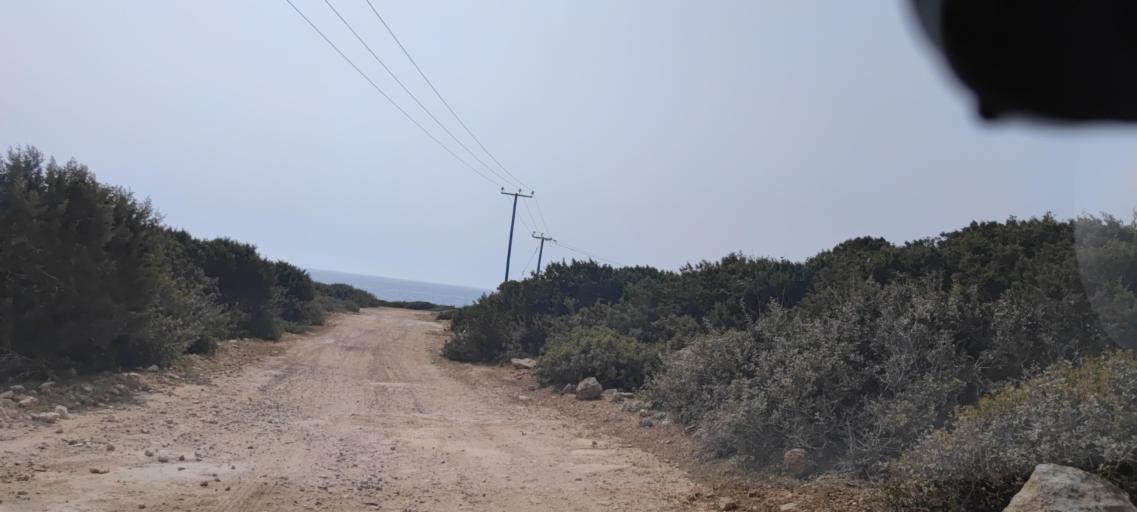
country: CY
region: Ammochostos
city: Rizokarpaso
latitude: 35.6788
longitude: 34.5771
